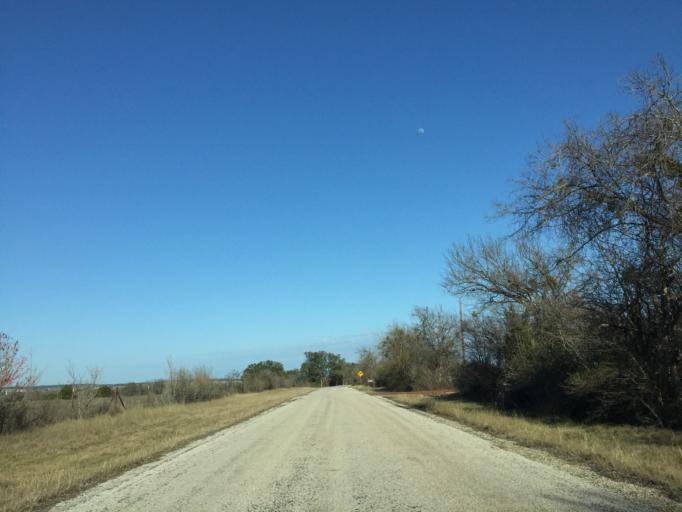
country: US
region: Texas
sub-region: Williamson County
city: Florence
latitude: 30.7764
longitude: -97.8425
